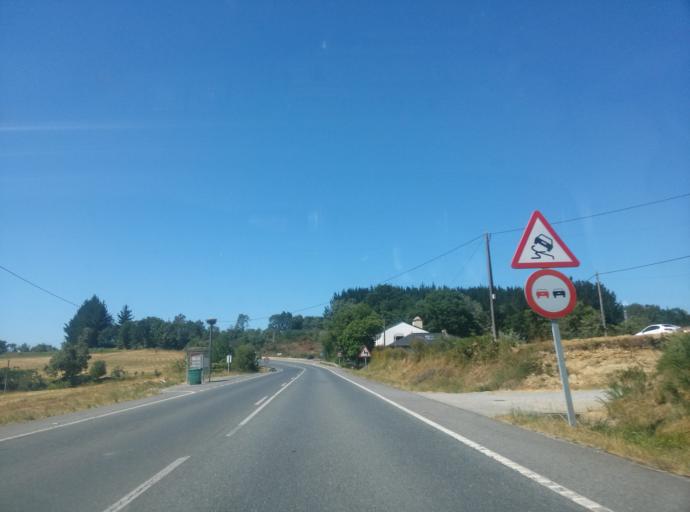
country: ES
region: Galicia
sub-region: Provincia de Lugo
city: Mos
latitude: 43.1236
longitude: -7.4858
